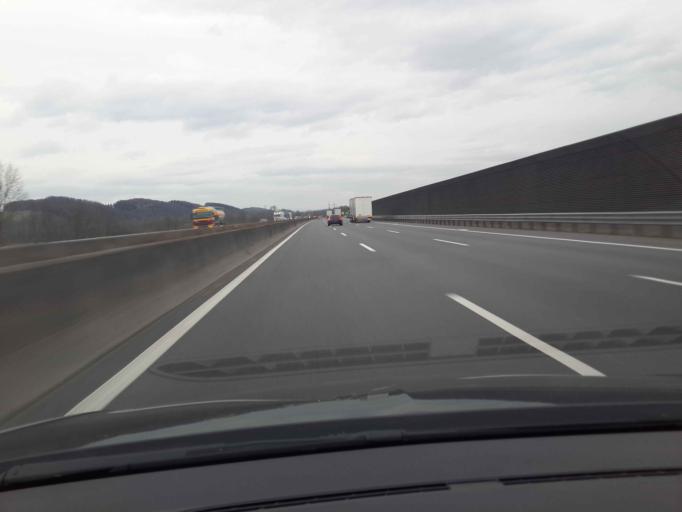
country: AT
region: Lower Austria
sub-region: Politischer Bezirk Melk
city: Neumarkt an der Ybbs
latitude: 48.1383
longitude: 15.0630
